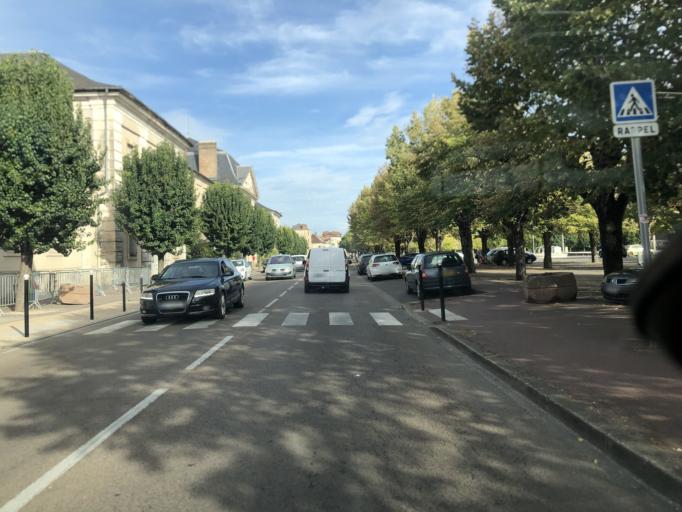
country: FR
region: Bourgogne
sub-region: Departement de l'Yonne
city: Joigny
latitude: 47.9812
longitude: 3.3983
